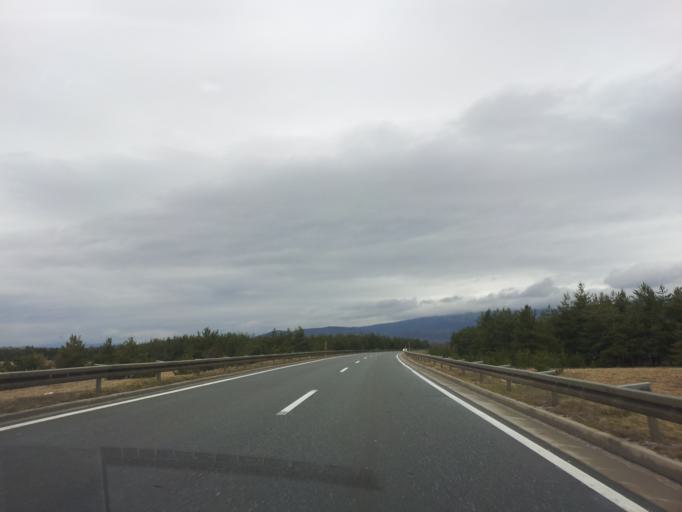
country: HR
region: Zadarska
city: Gracac
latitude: 44.5194
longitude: 15.7448
